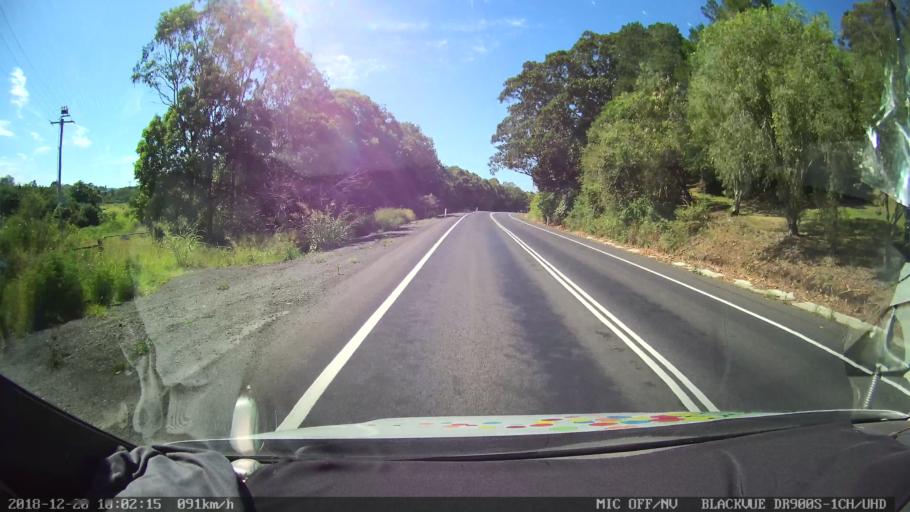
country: AU
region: New South Wales
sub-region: Lismore Municipality
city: East Lismore
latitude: -28.8555
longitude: 153.2612
